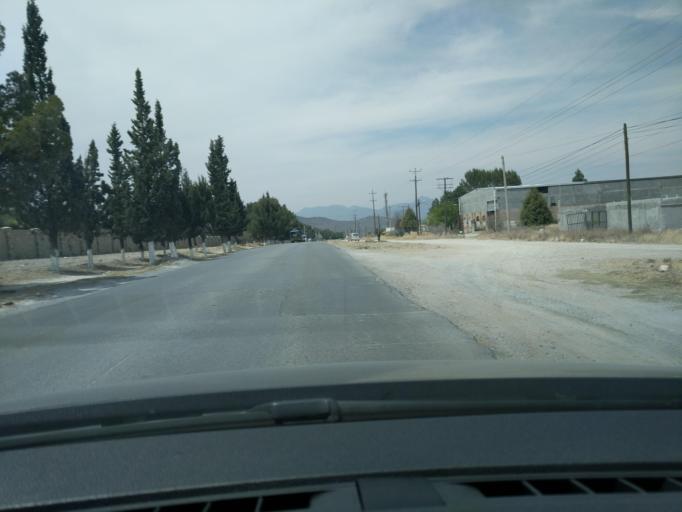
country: MX
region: Coahuila
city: Saltillo
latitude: 25.3550
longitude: -101.0287
